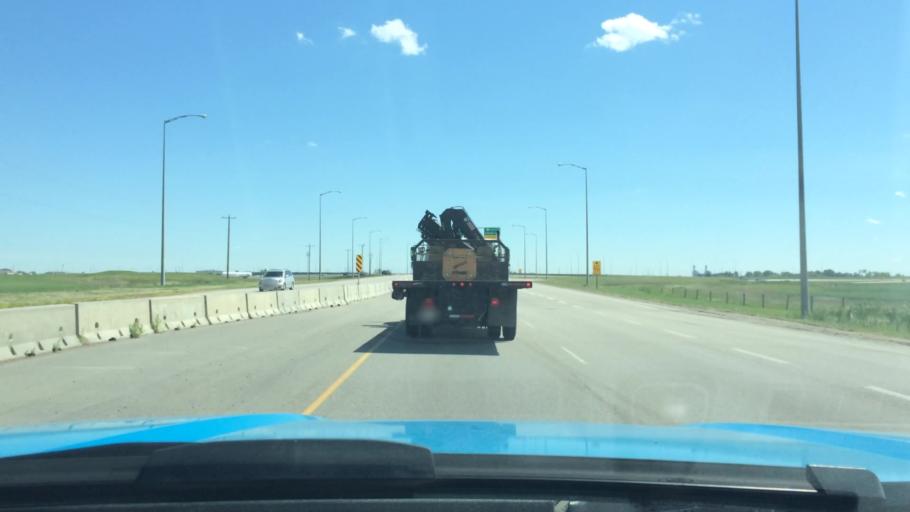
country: CA
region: Alberta
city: Chestermere
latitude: 50.9796
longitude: -113.9320
